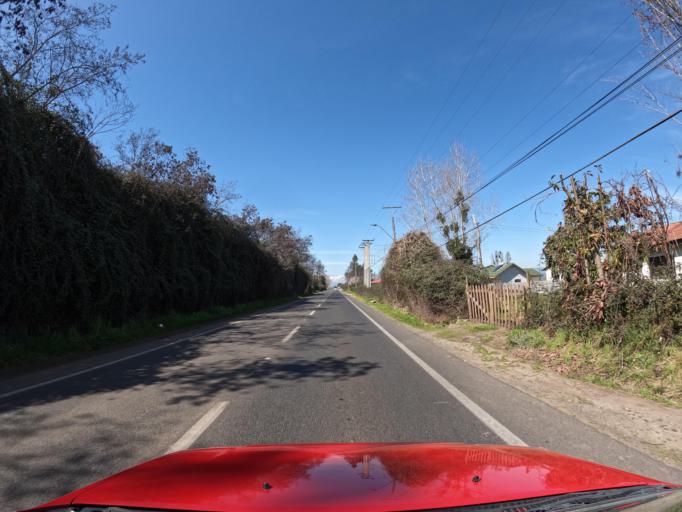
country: CL
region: Maule
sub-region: Provincia de Curico
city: Teno
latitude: -34.9641
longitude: -71.0622
